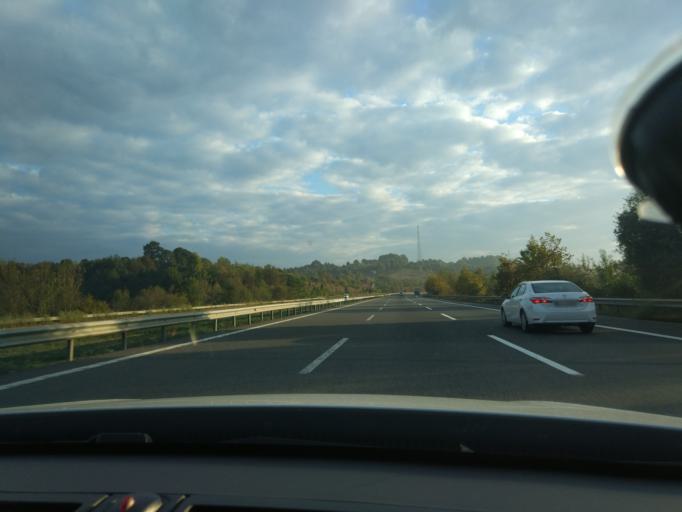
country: TR
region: Sakarya
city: Hendek
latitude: 40.7652
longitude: 30.7593
